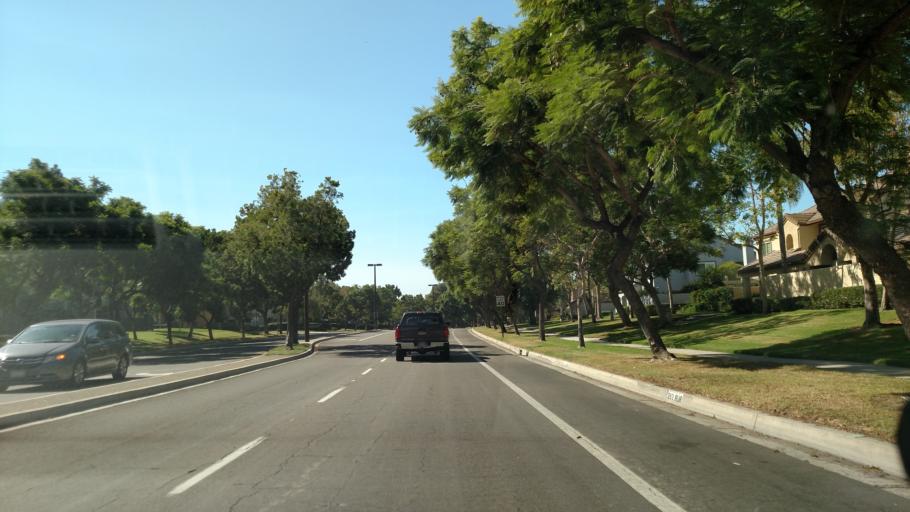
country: US
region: California
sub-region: Orange County
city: Irvine
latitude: 33.6710
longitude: -117.7917
